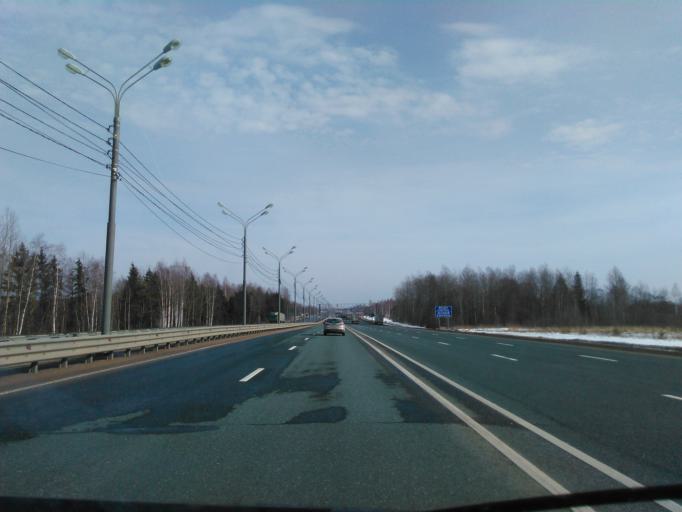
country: RU
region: Smolensk
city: Rudnya
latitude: 54.6910
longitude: 30.9934
